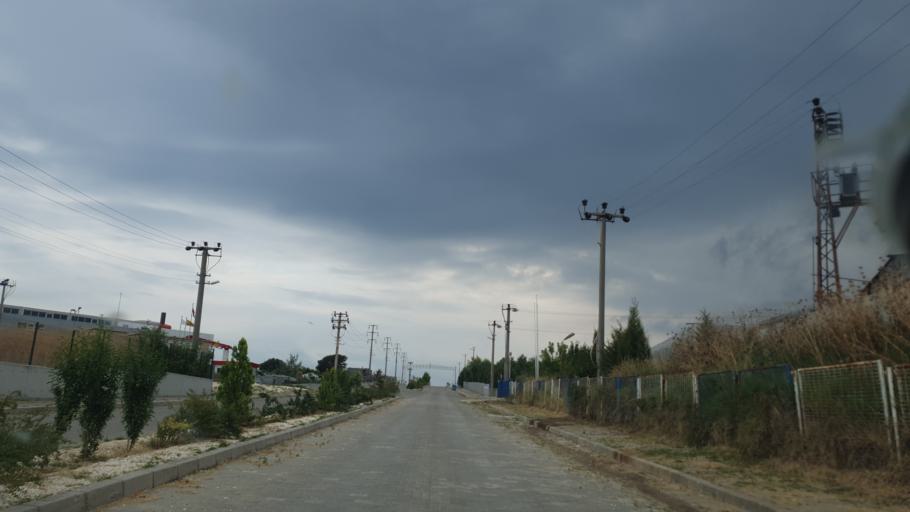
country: TR
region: Tekirdag
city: Hayrabolu
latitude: 41.2245
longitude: 27.0472
